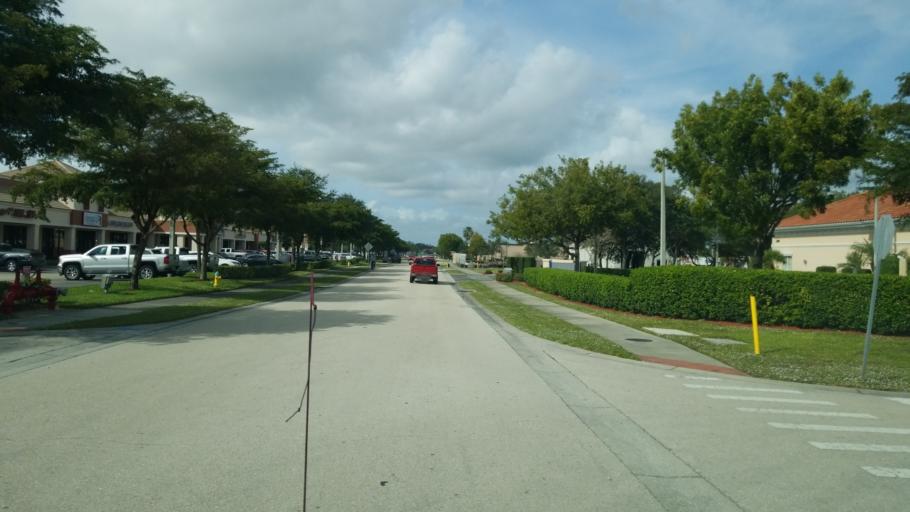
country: US
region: Florida
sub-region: Sarasota County
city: North Port
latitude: 27.0340
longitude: -82.2104
